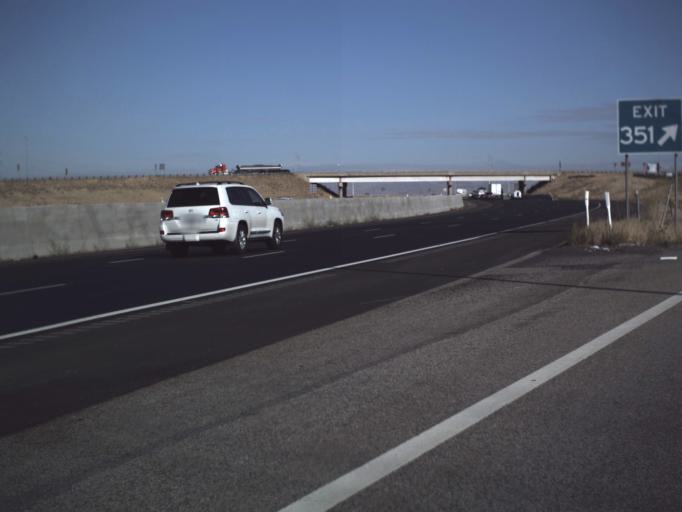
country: US
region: Utah
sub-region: Box Elder County
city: South Willard
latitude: 41.3380
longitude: -112.0346
